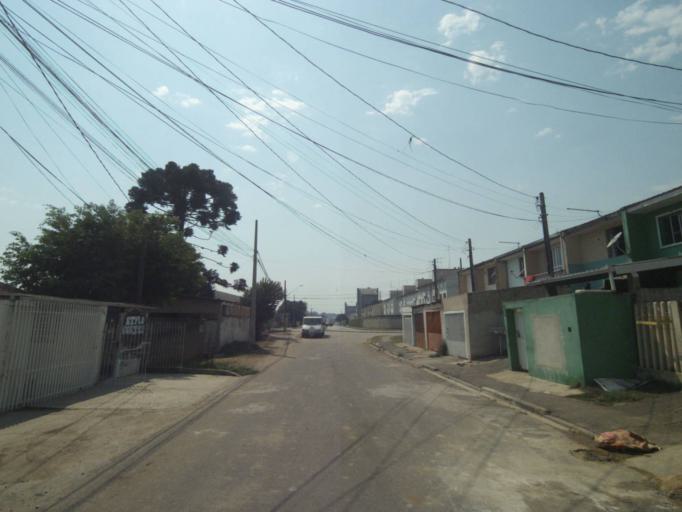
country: BR
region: Parana
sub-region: Curitiba
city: Curitiba
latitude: -25.4689
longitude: -49.2606
